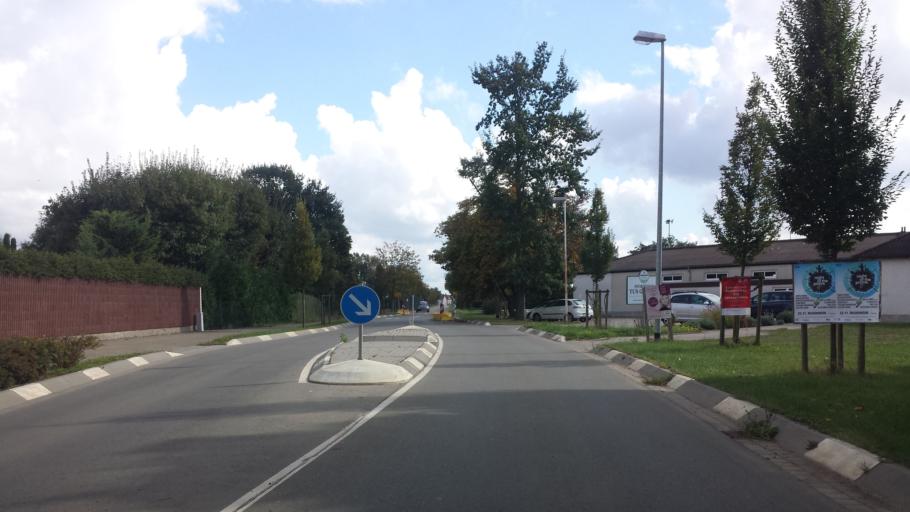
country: DE
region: Rheinland-Pfalz
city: Hochdorf-Assenheim
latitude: 49.4291
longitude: 8.2746
